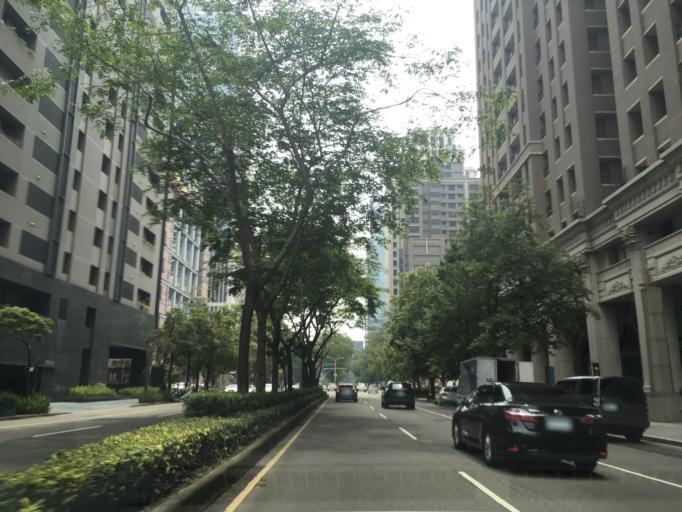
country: TW
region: Taiwan
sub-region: Taichung City
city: Taichung
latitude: 24.1649
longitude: 120.6412
